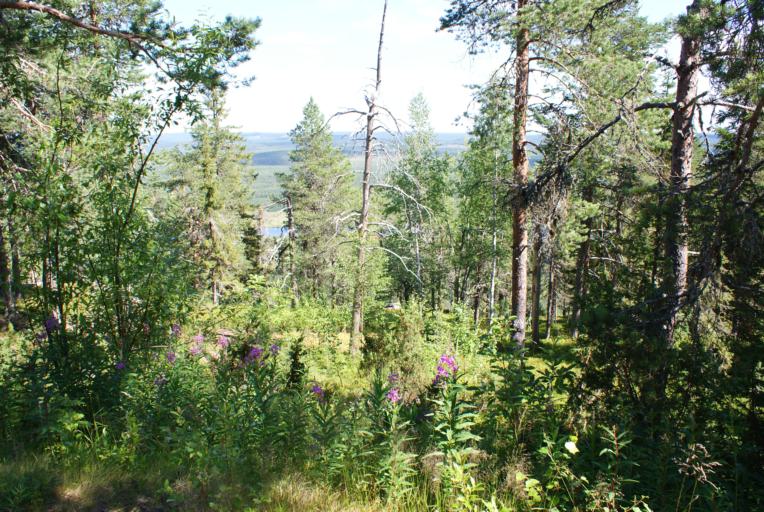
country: SE
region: Norrbotten
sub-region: Overtornea Kommun
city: OEvertornea
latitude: 66.3986
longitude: 23.7253
